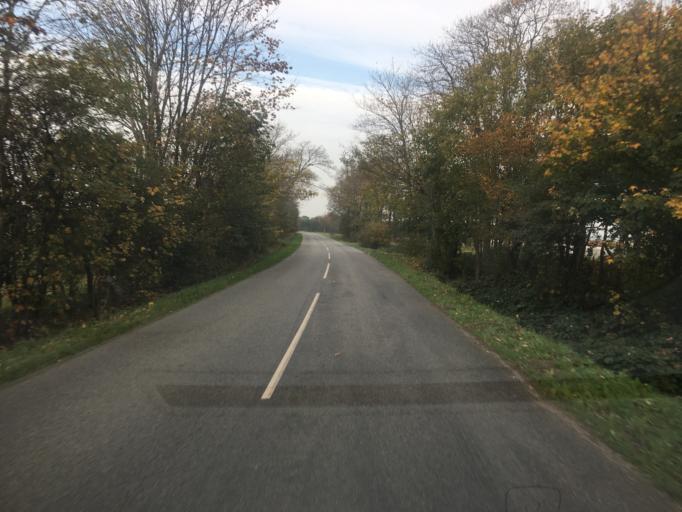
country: DK
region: South Denmark
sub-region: Tonder Kommune
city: Toftlund
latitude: 55.1111
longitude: 9.0870
